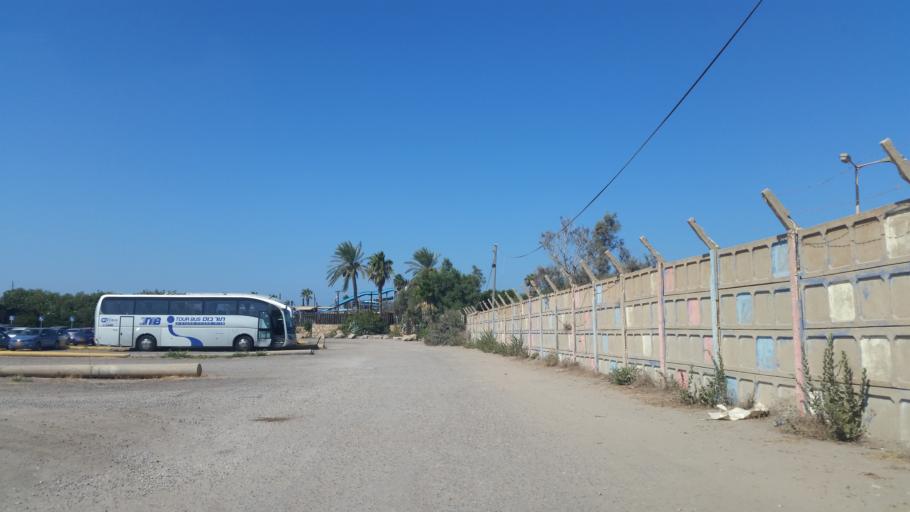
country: IL
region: Haifa
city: `Atlit
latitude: 32.6804
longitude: 34.9296
